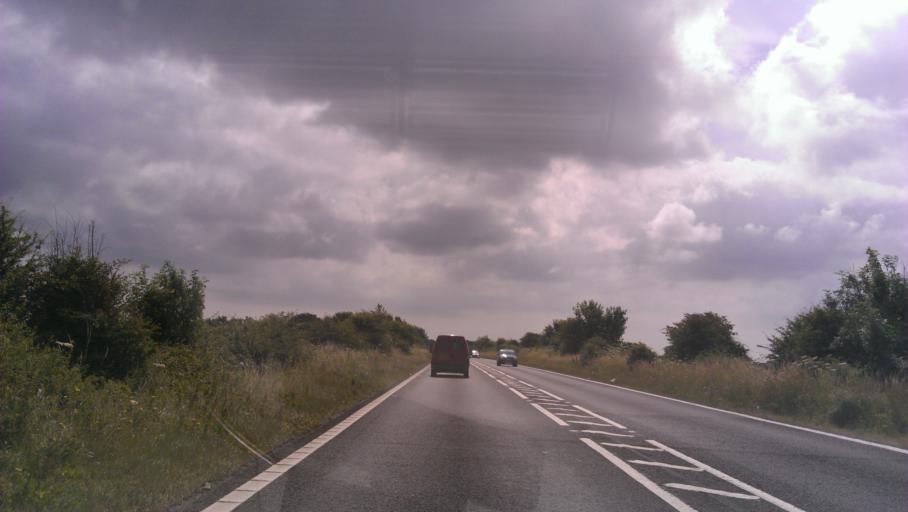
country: GB
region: England
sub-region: Kent
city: Shepherdswell
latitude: 51.1623
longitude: 1.2661
